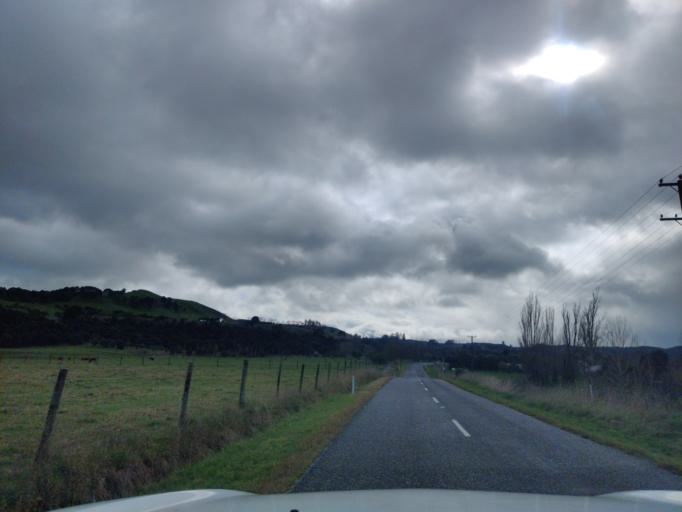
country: NZ
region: Manawatu-Wanganui
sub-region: Palmerston North City
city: Palmerston North
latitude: -40.1898
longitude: 175.7817
